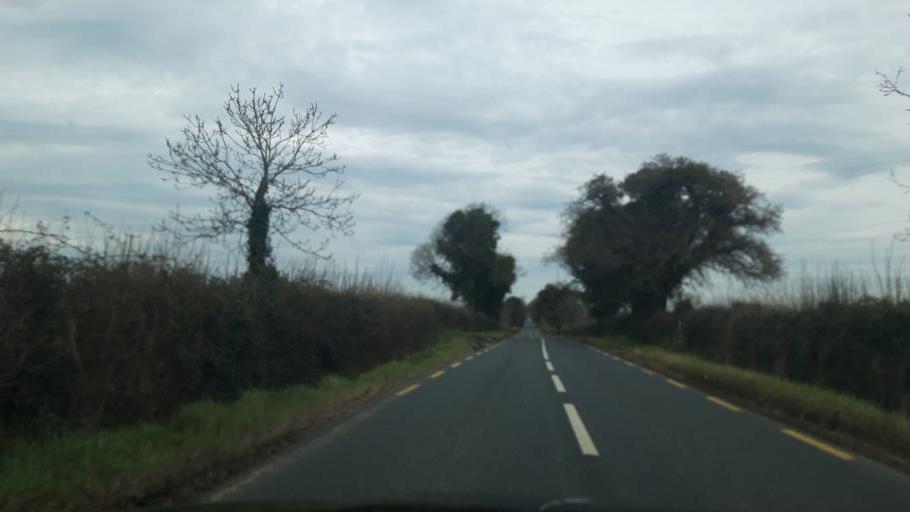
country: IE
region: Leinster
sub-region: Kildare
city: Clane
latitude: 53.3144
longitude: -6.7119
